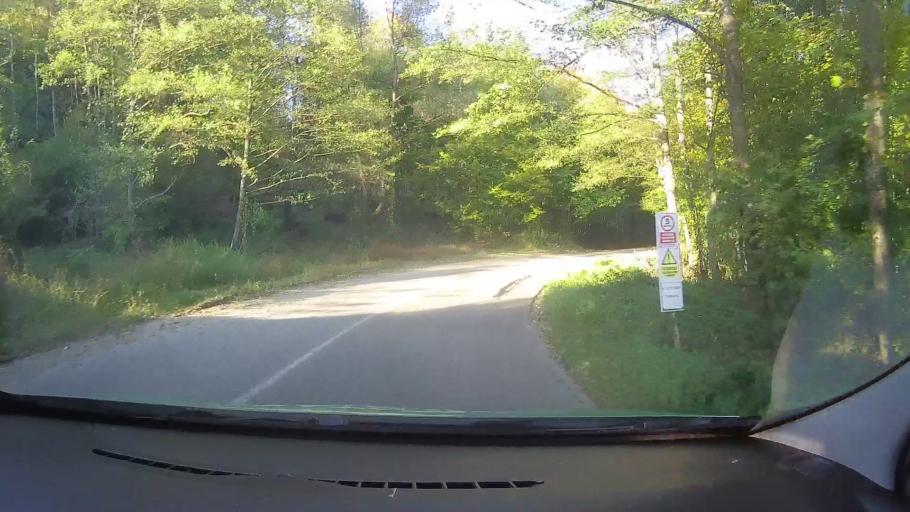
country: RO
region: Timis
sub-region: Comuna Nadrag
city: Nadrag
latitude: 45.6696
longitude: 22.1654
